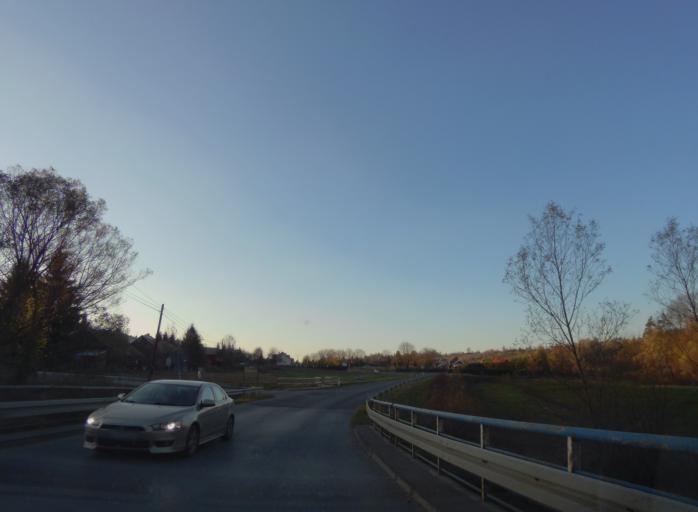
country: PL
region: Subcarpathian Voivodeship
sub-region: Powiat leski
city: Polanczyk
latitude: 49.3890
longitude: 22.3940
